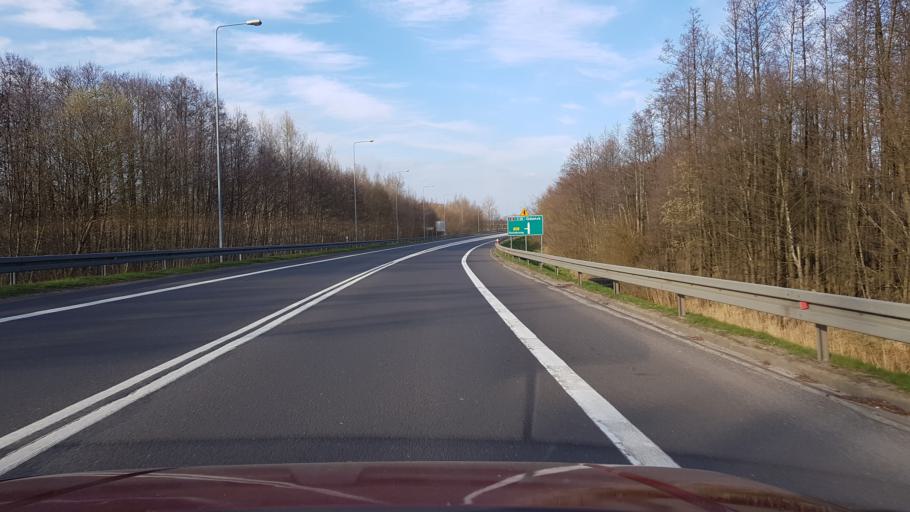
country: PL
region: West Pomeranian Voivodeship
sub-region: Powiat bialogardzki
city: Karlino
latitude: 54.0453
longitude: 15.8994
